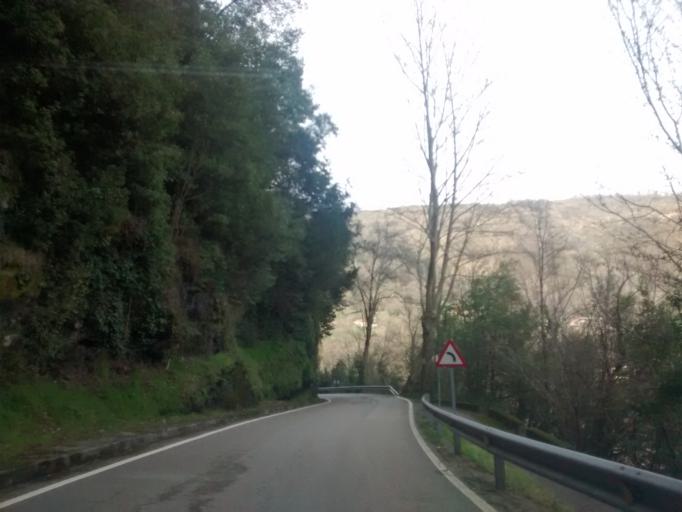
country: ES
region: Cantabria
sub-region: Provincia de Cantabria
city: San Pedro del Romeral
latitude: 43.1717
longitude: -3.8687
